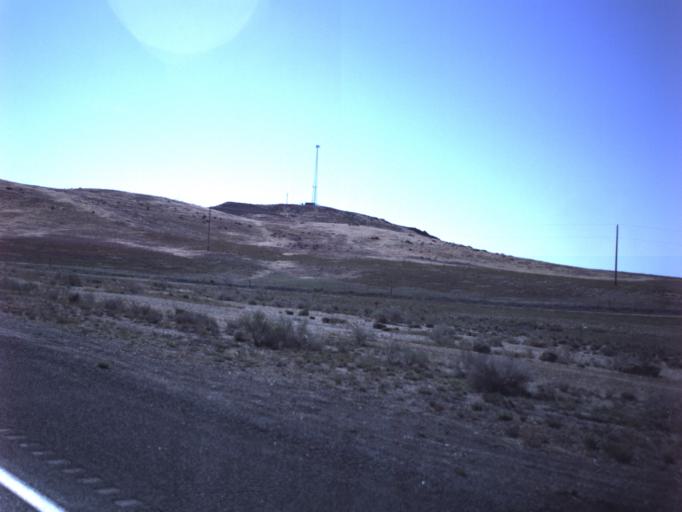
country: US
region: Utah
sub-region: Sanpete County
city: Gunnison
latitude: 39.1745
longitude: -111.8365
